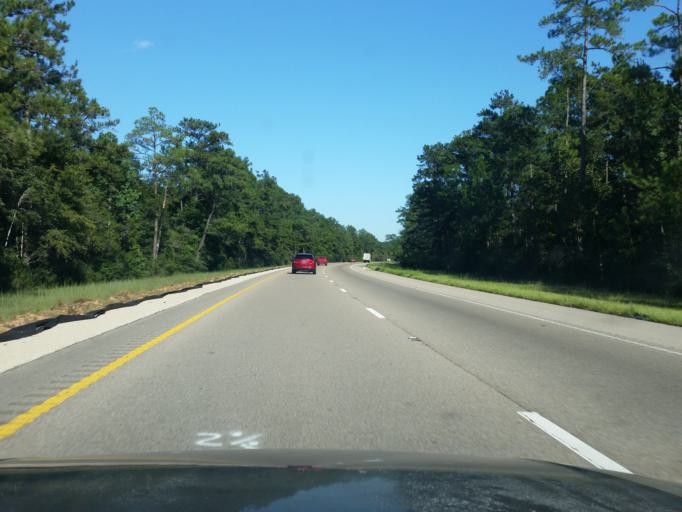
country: US
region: Mississippi
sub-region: Hancock County
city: Pearlington
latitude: 30.3327
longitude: -89.5387
